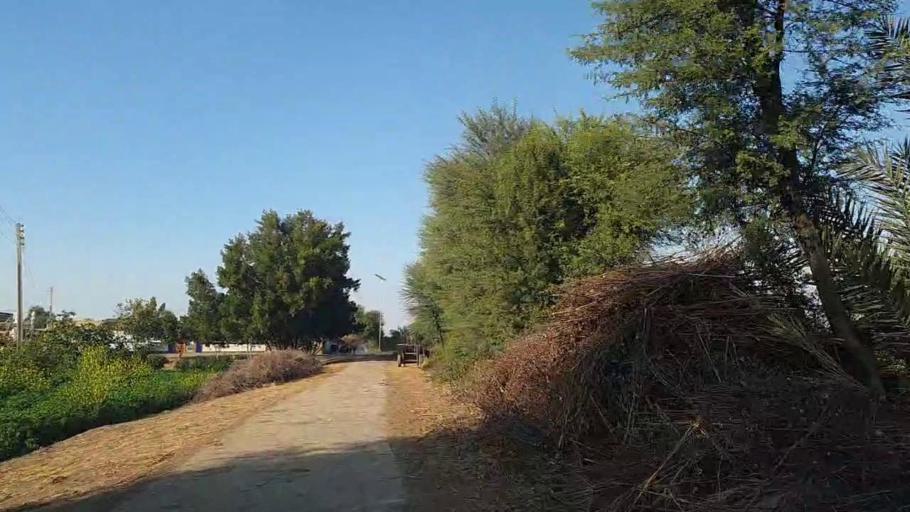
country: PK
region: Sindh
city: Shahpur Chakar
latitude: 26.1967
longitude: 68.6336
